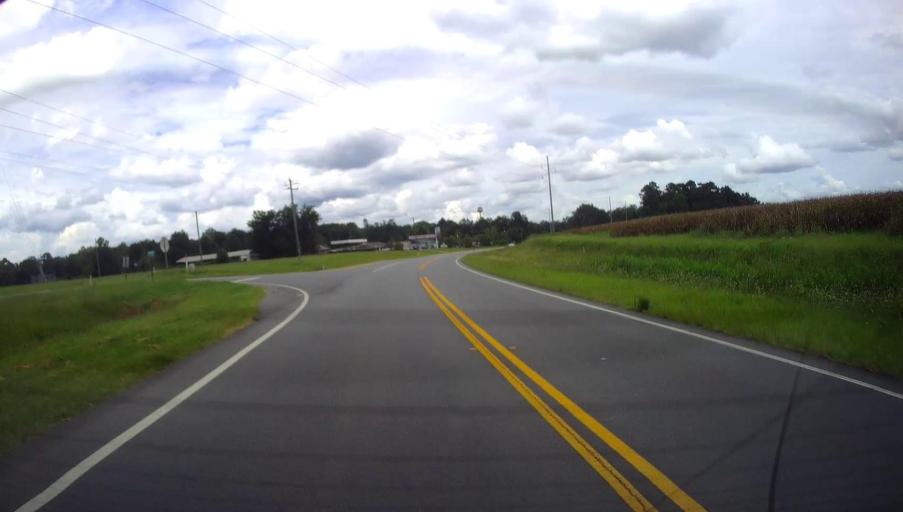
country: US
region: Georgia
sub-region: Macon County
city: Oglethorpe
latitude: 32.2897
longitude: -84.0554
